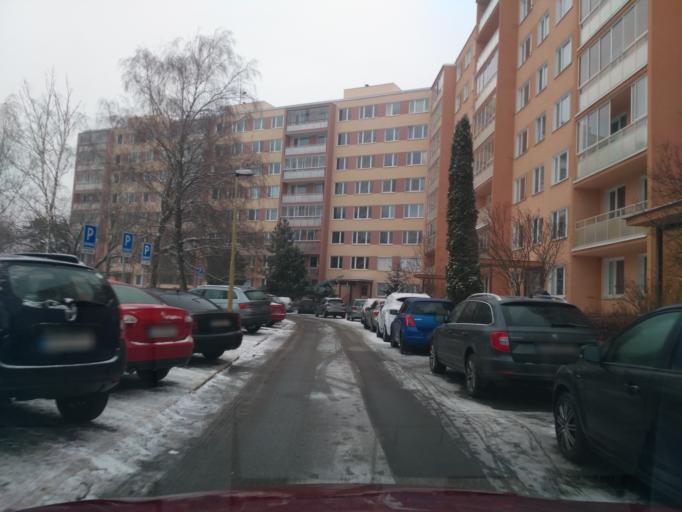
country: SK
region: Kosicky
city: Kosice
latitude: 48.7071
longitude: 21.2328
